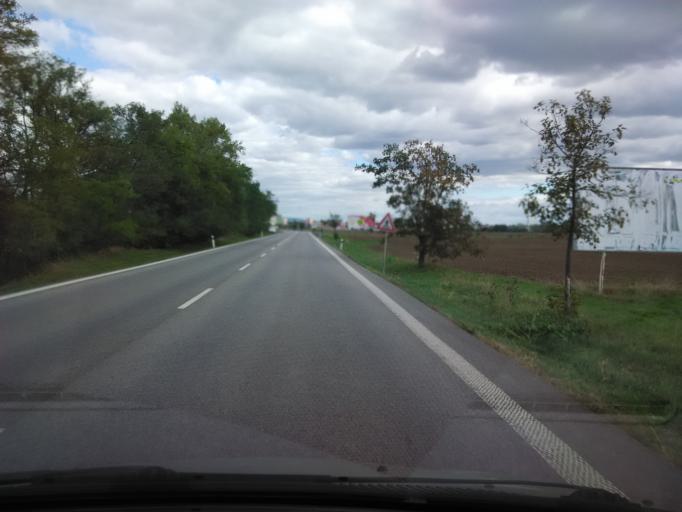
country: SK
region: Nitriansky
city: Levice
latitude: 48.2020
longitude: 18.5653
